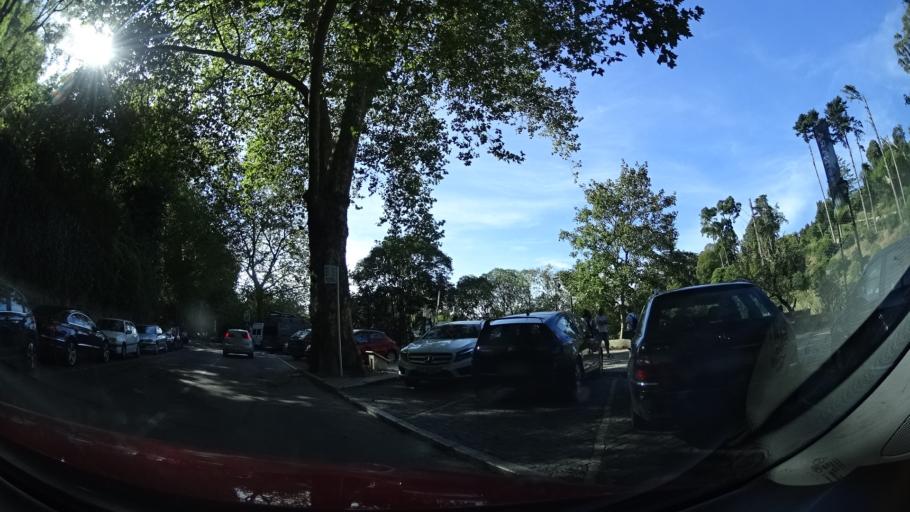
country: PT
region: Lisbon
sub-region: Sintra
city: Sintra
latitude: 38.7970
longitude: -9.3873
